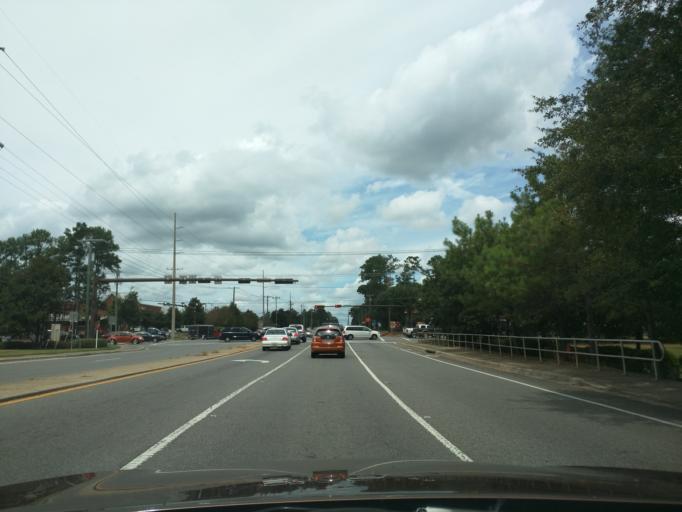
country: US
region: Florida
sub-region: Leon County
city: Tallahassee
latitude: 30.5605
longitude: -84.2170
